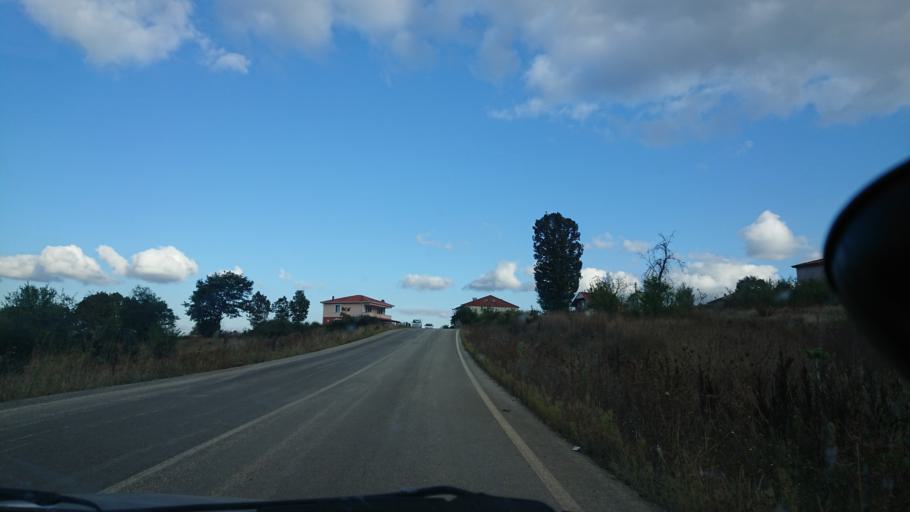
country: TR
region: Bilecik
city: Pazaryeri
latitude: 40.0106
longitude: 29.8031
